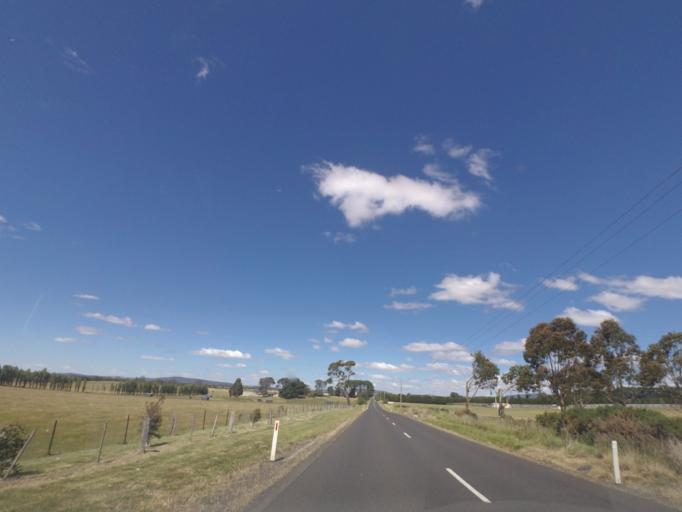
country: AU
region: Victoria
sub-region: Mount Alexander
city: Castlemaine
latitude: -37.2874
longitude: 144.4505
